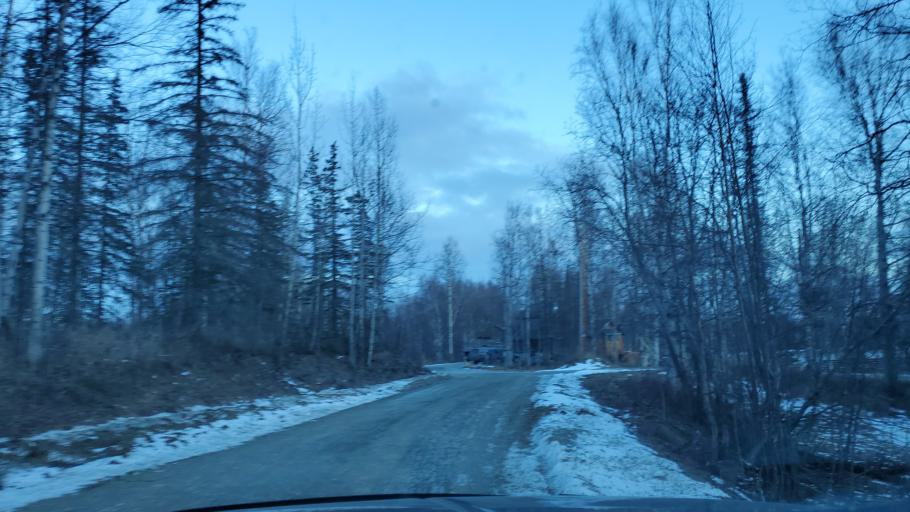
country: US
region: Alaska
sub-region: Matanuska-Susitna Borough
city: Lakes
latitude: 61.6641
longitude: -149.3240
